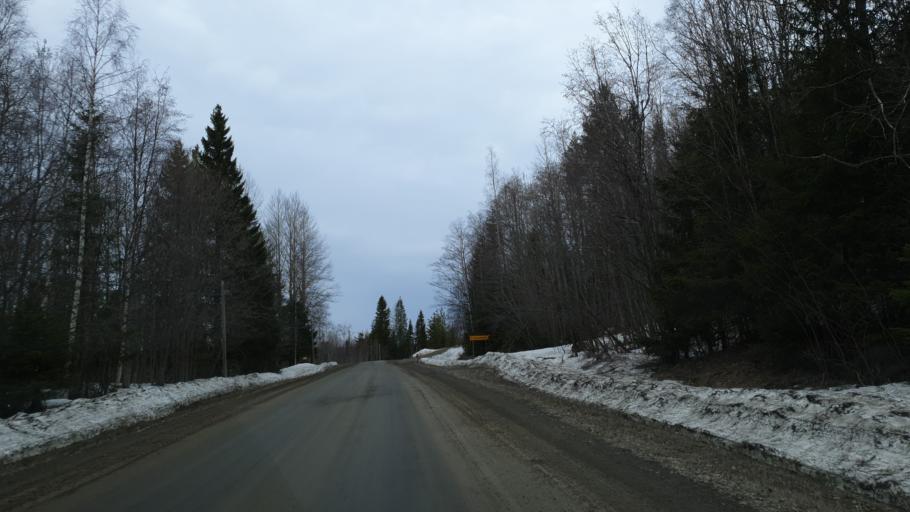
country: SE
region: Vaesterbotten
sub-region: Skelleftea Kommun
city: Burea
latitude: 64.3216
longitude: 21.1386
